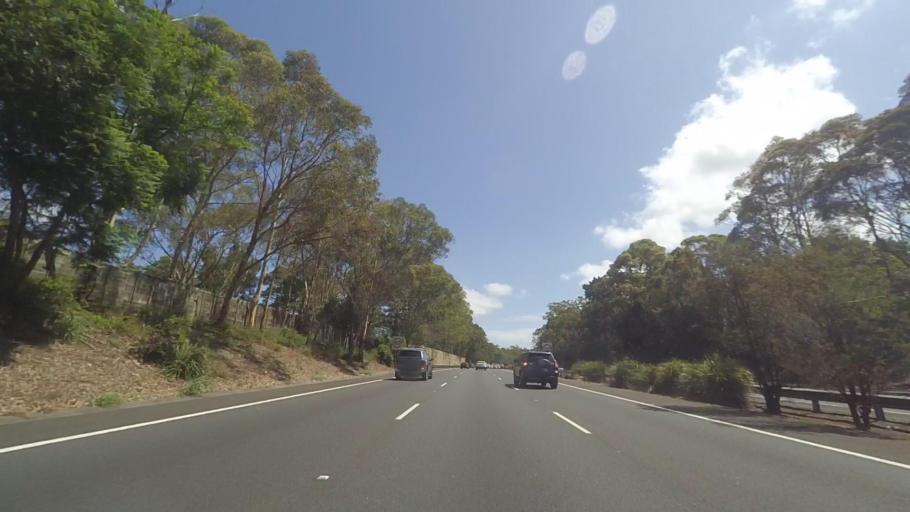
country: AU
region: New South Wales
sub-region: Ku-ring-gai
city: North Wahroonga
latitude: -33.7099
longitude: 151.1167
